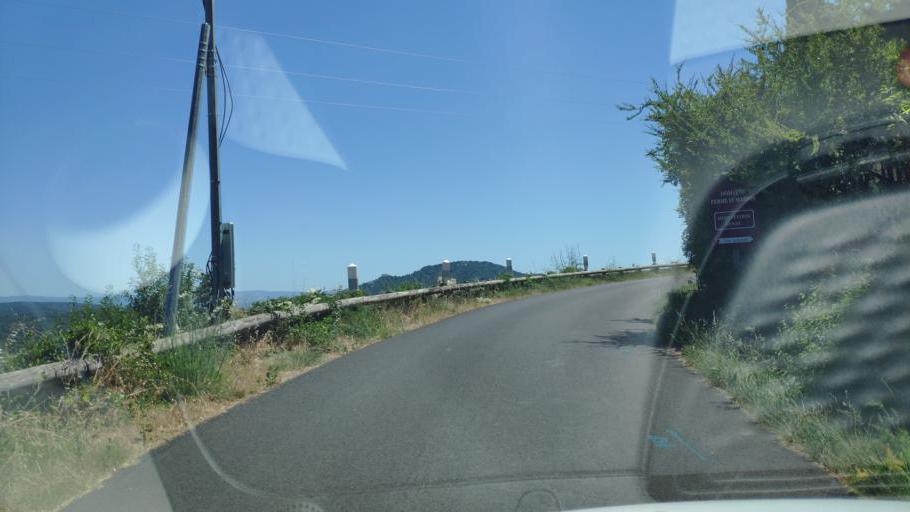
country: FR
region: Provence-Alpes-Cote d'Azur
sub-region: Departement du Vaucluse
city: Malaucene
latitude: 44.1711
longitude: 5.0707
